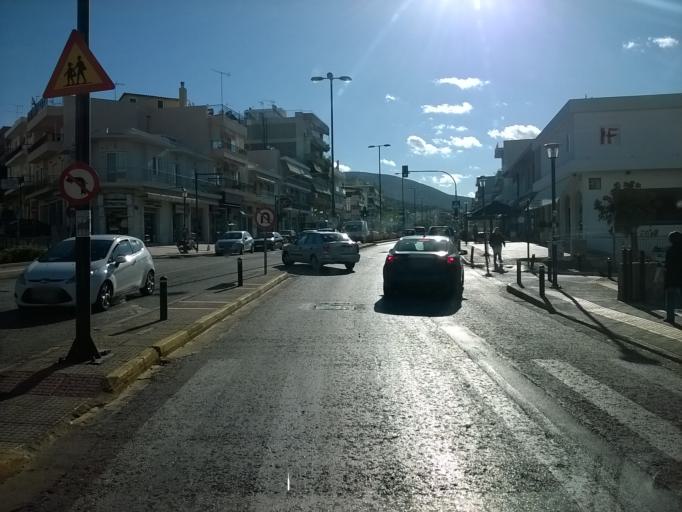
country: GR
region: Attica
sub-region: Nomarchia Athinas
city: Argyroupoli
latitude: 37.9133
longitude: 23.7480
